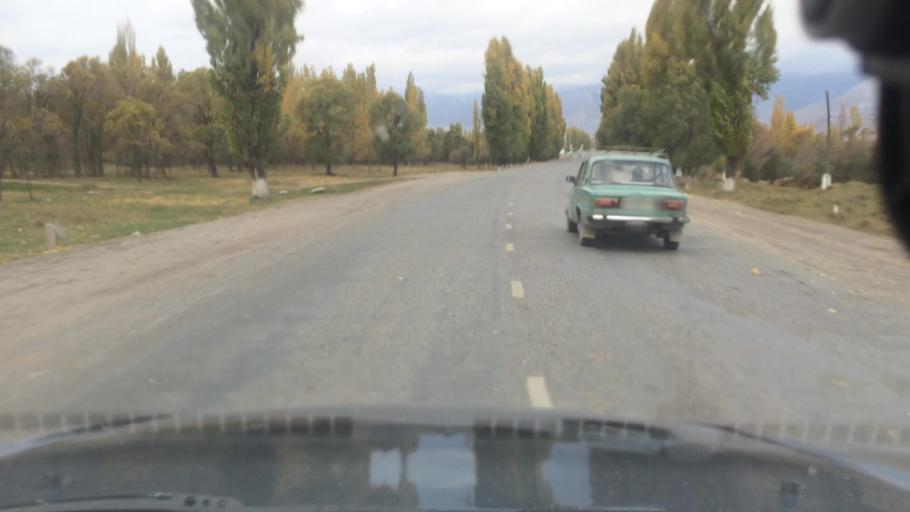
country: KG
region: Ysyk-Koel
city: Tyup
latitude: 42.7350
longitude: 78.3518
